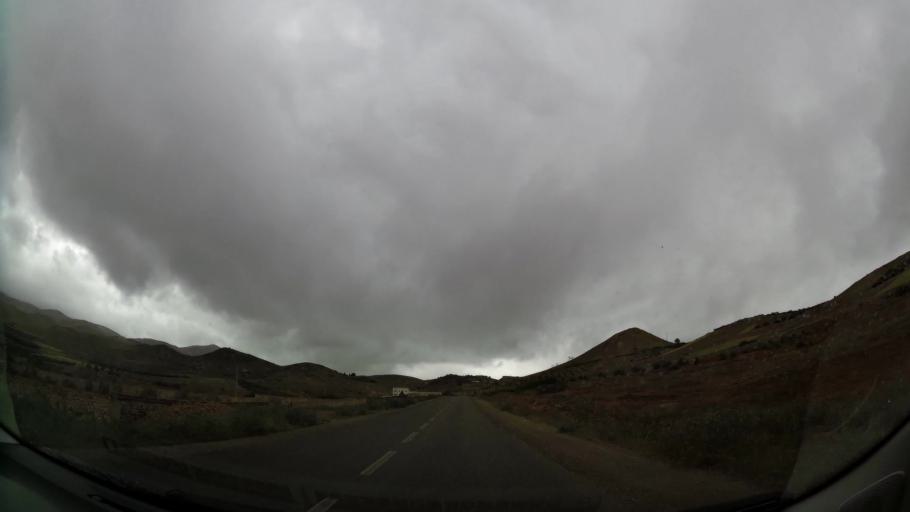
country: MA
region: Oriental
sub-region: Nador
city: Midar
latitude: 35.0606
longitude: -3.4688
